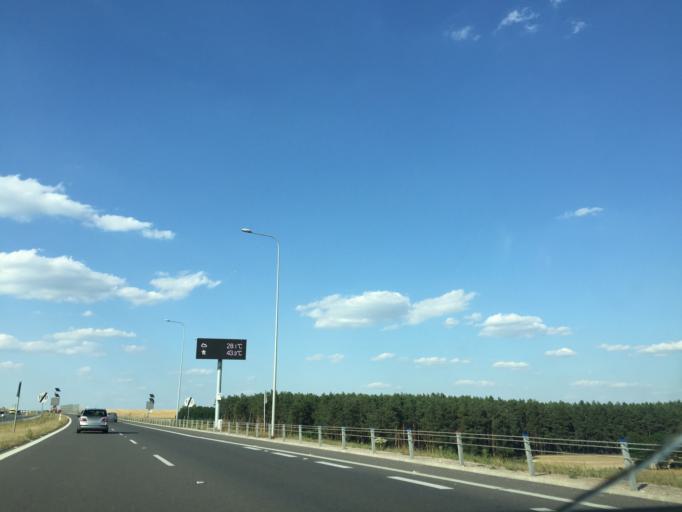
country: PL
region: Swietokrzyskie
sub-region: Powiat jedrzejowski
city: Sobkow
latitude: 50.7077
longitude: 20.4045
